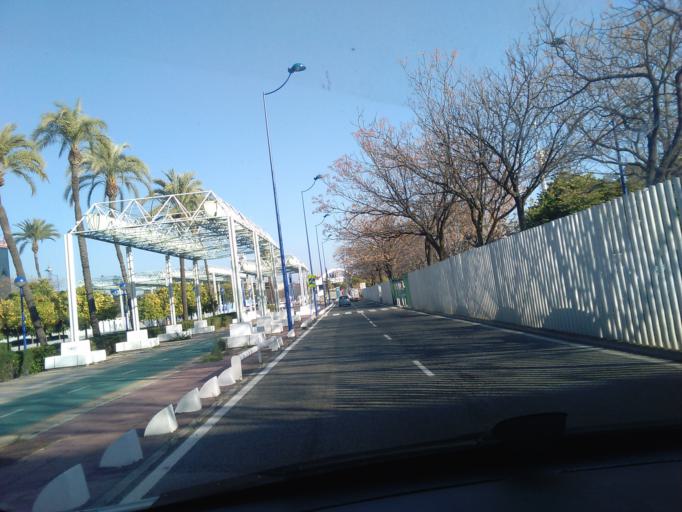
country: ES
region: Andalusia
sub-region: Provincia de Sevilla
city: Camas
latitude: 37.4058
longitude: -6.0051
